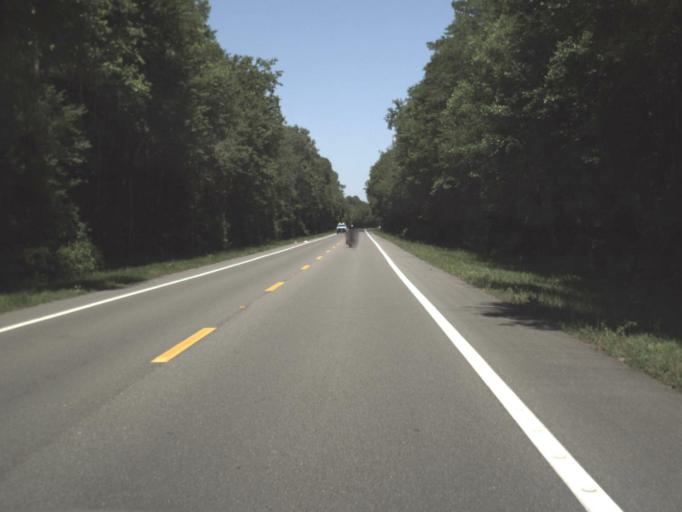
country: US
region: Florida
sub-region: Baker County
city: Macclenny
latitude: 30.2605
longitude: -82.2425
